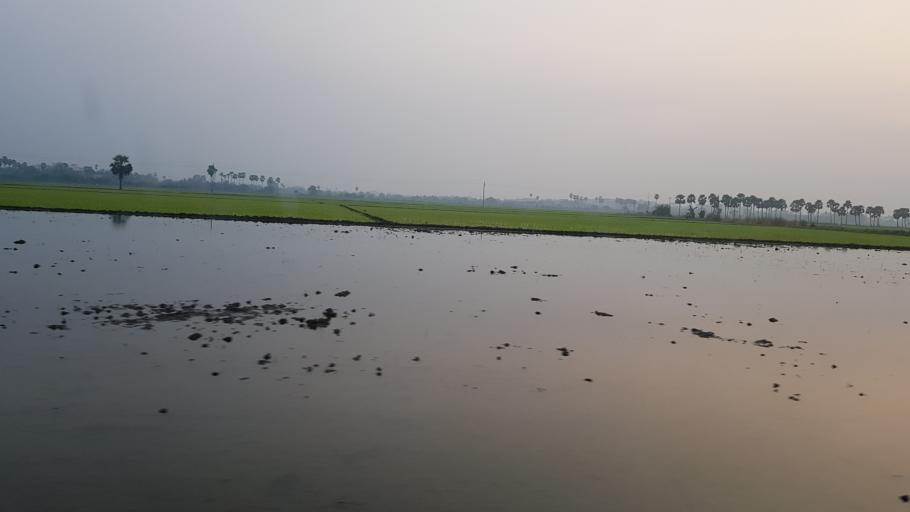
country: IN
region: Andhra Pradesh
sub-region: Krishna
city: Kankipadu
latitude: 16.4564
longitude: 80.7690
